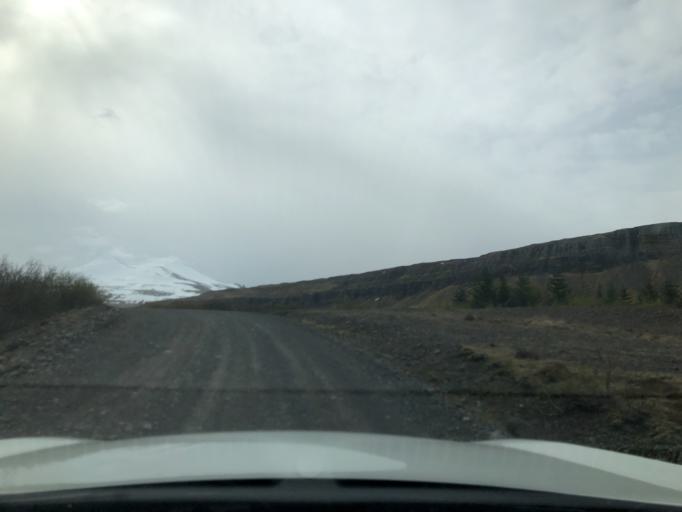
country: IS
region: South
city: Hveragerdi
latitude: 64.3855
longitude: -21.3092
